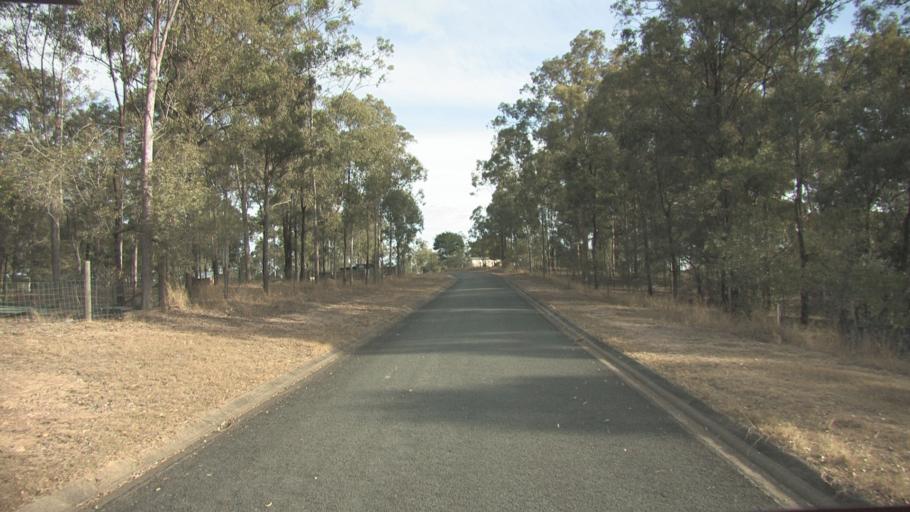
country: AU
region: Queensland
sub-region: Logan
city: Cedar Vale
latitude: -27.8785
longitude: 153.0349
